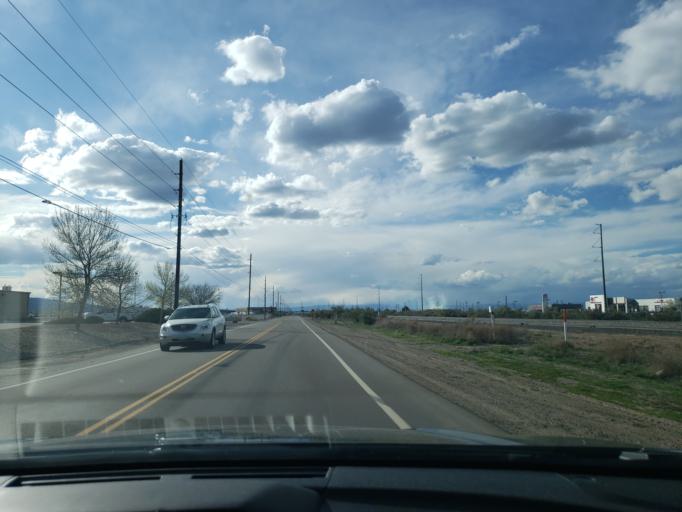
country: US
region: Colorado
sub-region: Mesa County
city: Redlands
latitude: 39.1031
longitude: -108.6328
